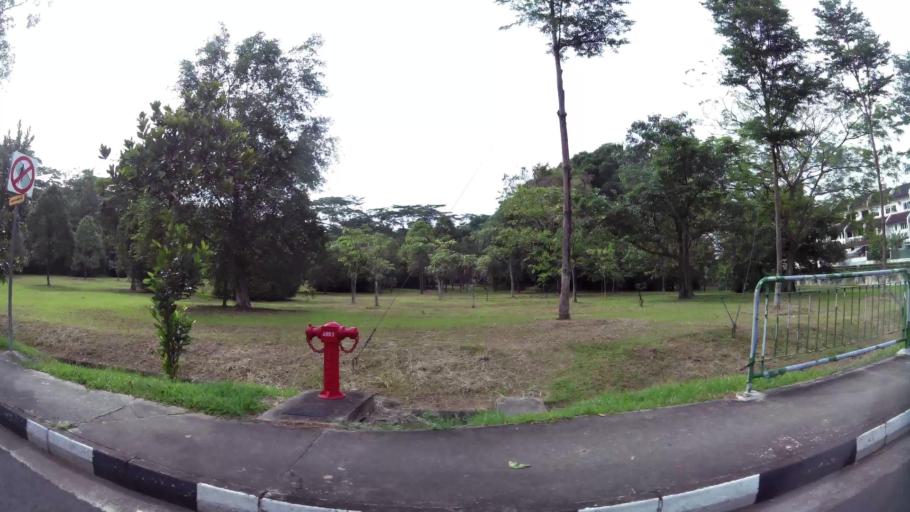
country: SG
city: Singapore
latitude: 1.3246
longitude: 103.7924
